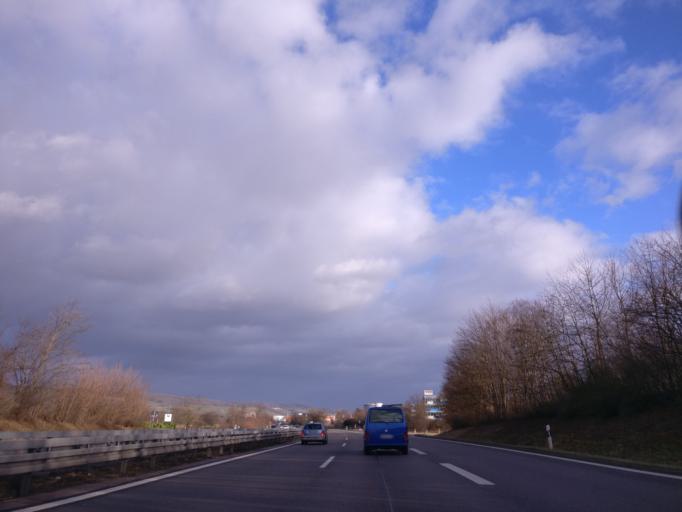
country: DE
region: Baden-Wuerttemberg
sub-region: Regierungsbezirk Stuttgart
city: Weinstadt-Endersbach
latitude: 48.8139
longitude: 9.3472
